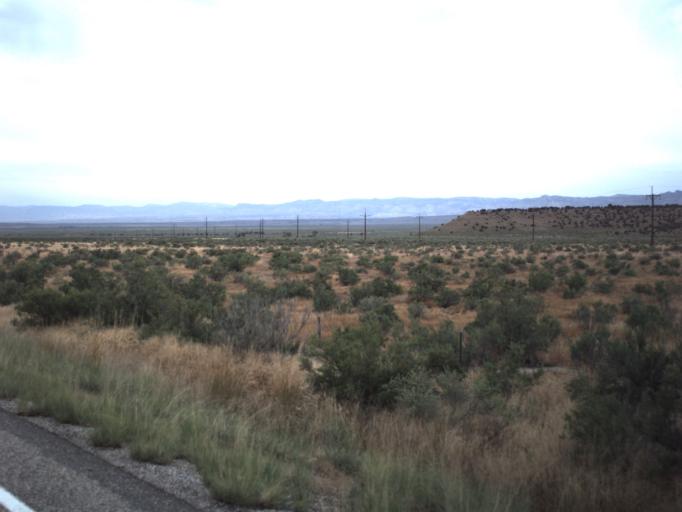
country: US
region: Utah
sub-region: Carbon County
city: East Carbon City
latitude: 39.5359
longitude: -110.4918
